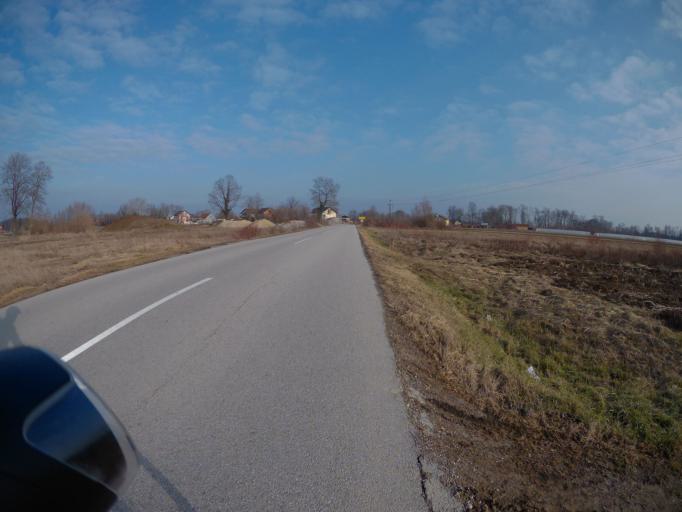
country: HR
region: Zagrebacka
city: Micevec
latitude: 45.7474
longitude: 16.1122
